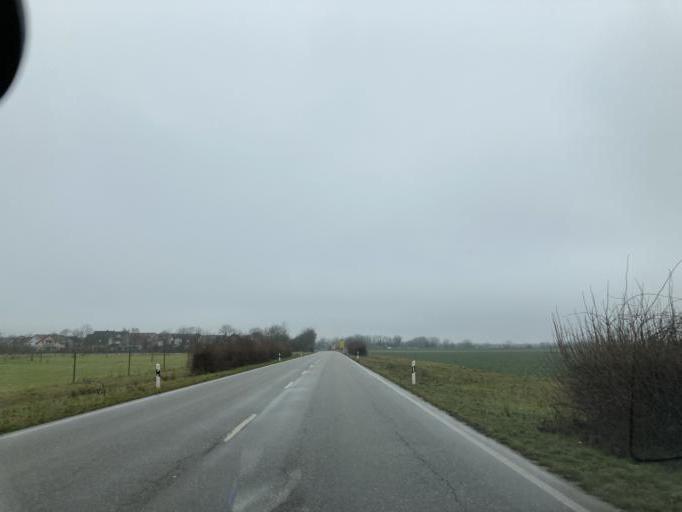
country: DE
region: Baden-Wuerttemberg
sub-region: Freiburg Region
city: Neuenburg am Rhein
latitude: 47.8185
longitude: 7.5771
